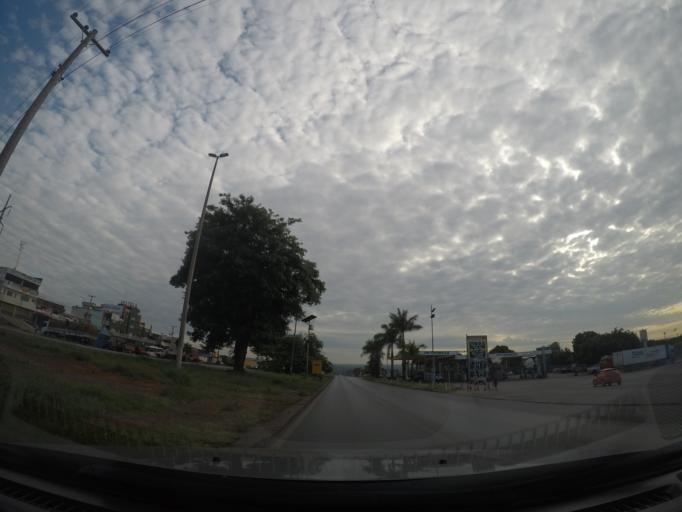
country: BR
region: Goias
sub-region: Planaltina
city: Planaltina
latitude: -15.6016
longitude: -47.6815
